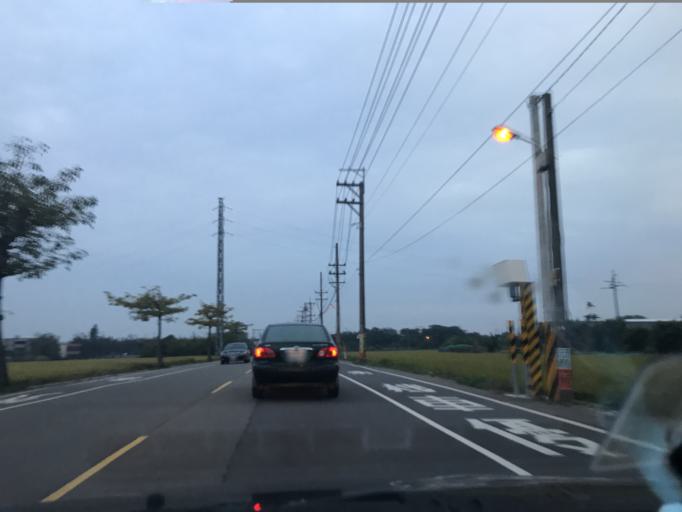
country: TW
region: Taiwan
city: Daxi
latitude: 24.9146
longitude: 121.2312
